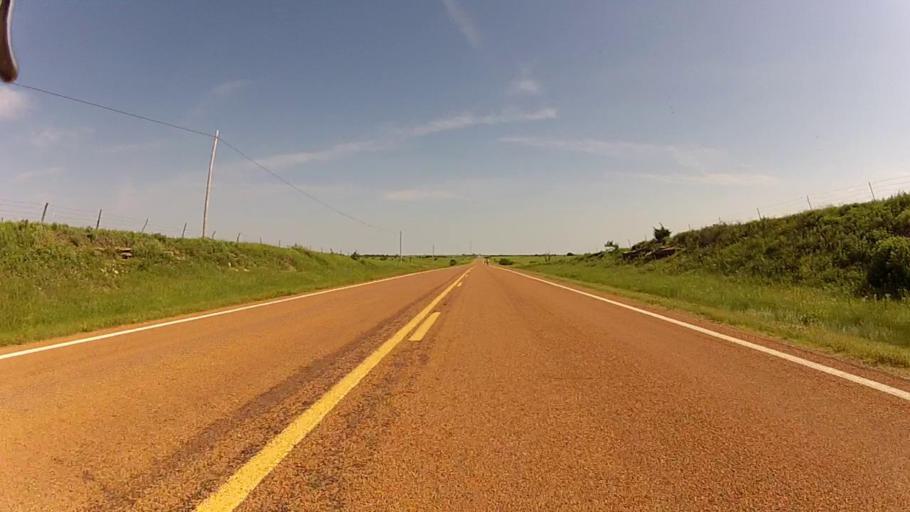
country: US
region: Kansas
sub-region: Cowley County
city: Winfield
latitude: 37.0864
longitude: -96.6433
